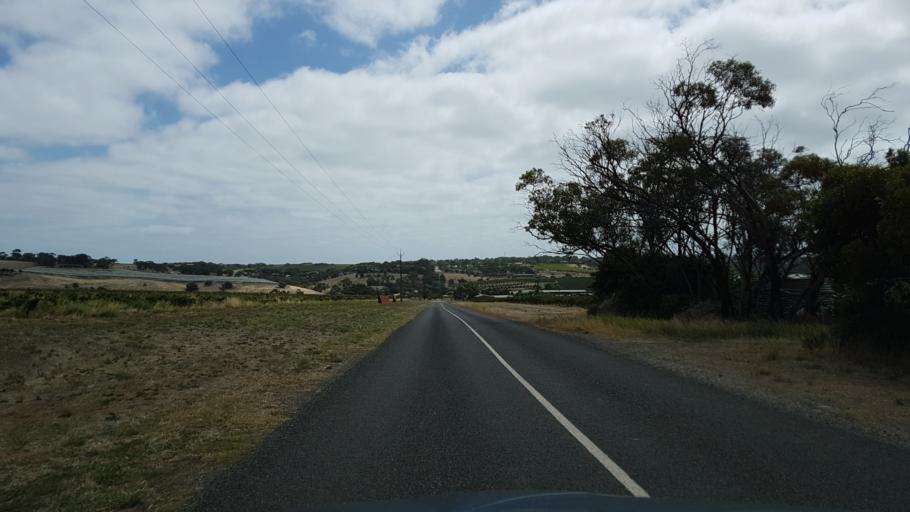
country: AU
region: South Australia
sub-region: Onkaparinga
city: McLaren Vale
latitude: -35.2140
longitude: 138.5176
